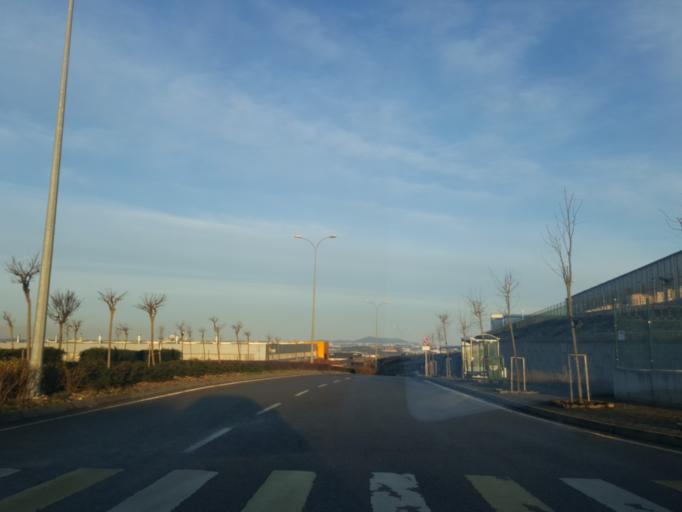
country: TR
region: Kocaeli
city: Tavsanli
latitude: 40.8311
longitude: 29.5577
